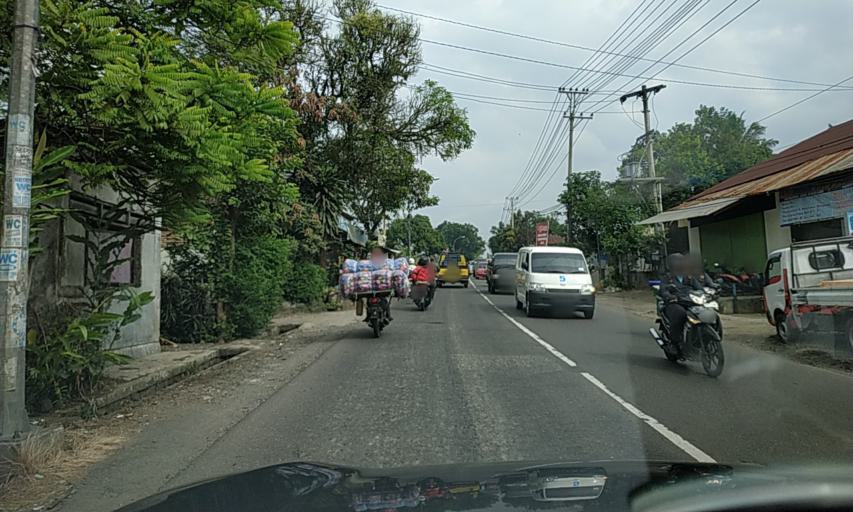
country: ID
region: Central Java
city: Purwokerto
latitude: -7.4185
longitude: 109.1868
